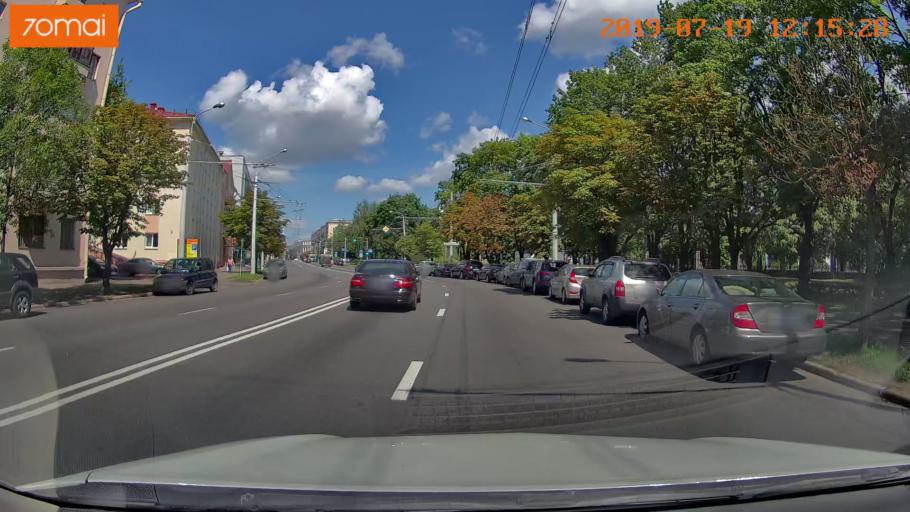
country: BY
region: Minsk
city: Minsk
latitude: 53.9181
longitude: 27.6038
